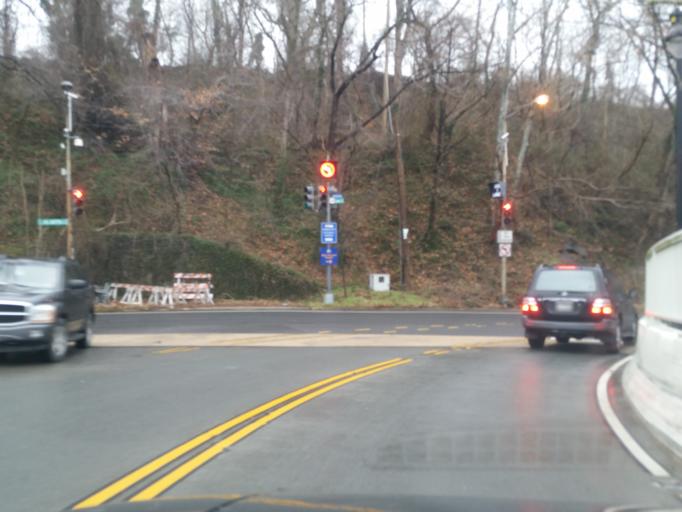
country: US
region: Maryland
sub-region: Montgomery County
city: Brookmont
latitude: 38.9303
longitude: -77.1121
